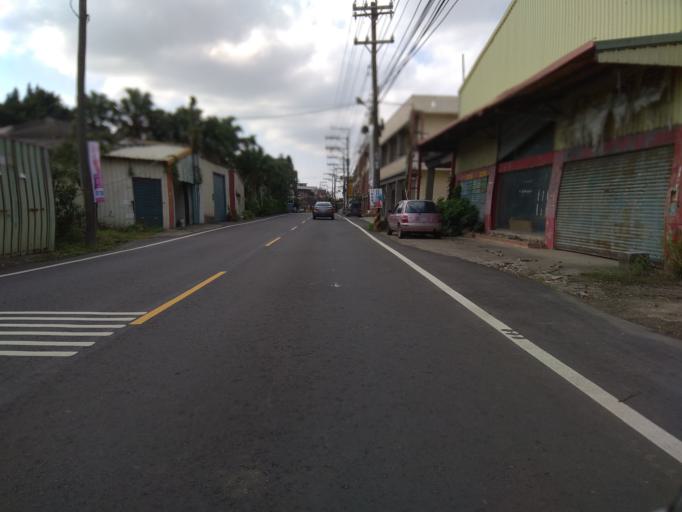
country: TW
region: Taiwan
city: Taoyuan City
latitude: 25.0597
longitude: 121.2331
